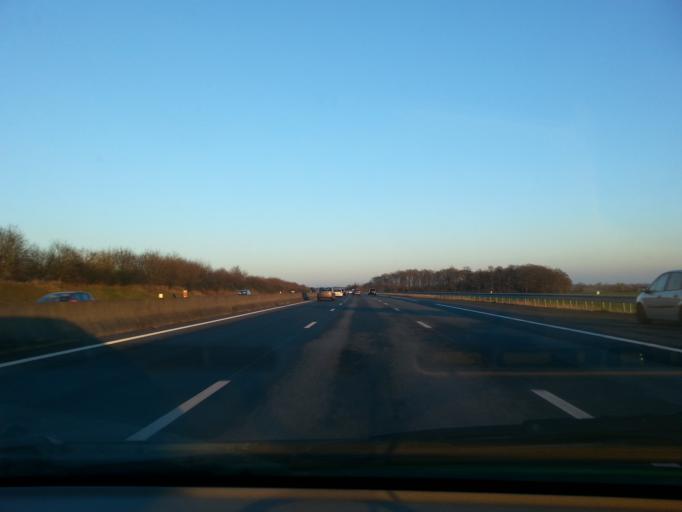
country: FR
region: Centre
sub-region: Departement d'Eure-et-Loir
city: Unverre
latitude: 48.2287
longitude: 1.0071
